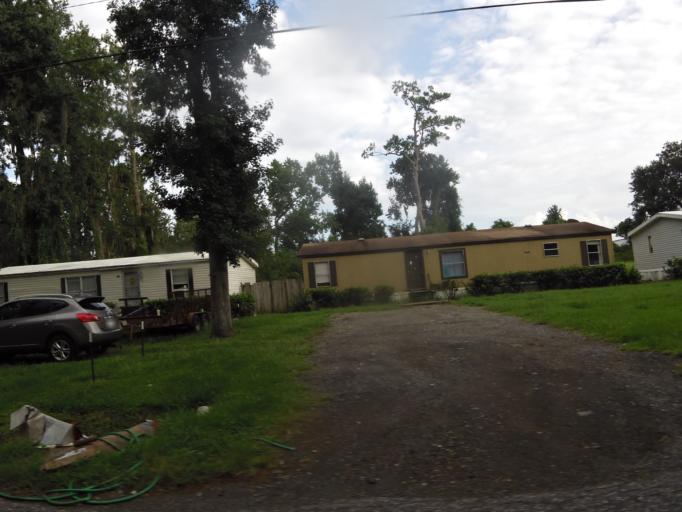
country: US
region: Florida
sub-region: Nassau County
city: Nassau Village-Ratliff
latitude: 30.4339
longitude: -81.7629
